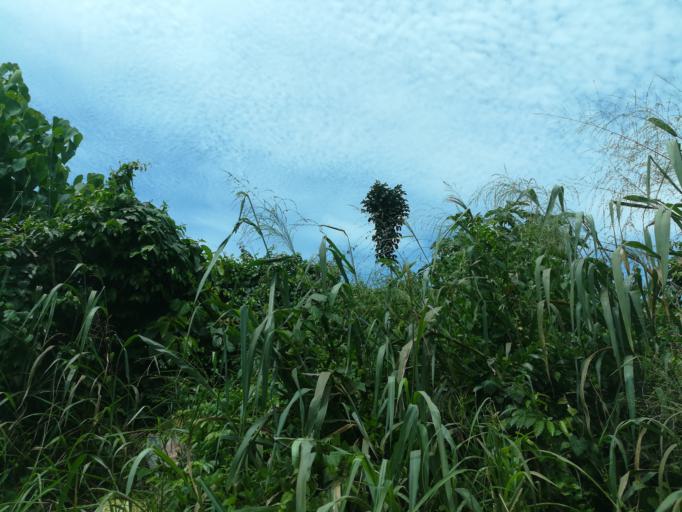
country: NG
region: Lagos
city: Ebute Ikorodu
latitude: 6.5763
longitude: 3.4894
